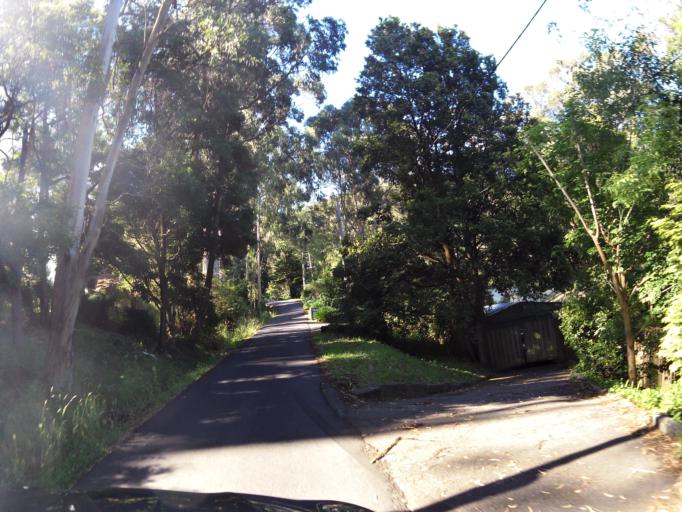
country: AU
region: Victoria
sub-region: Yarra Ranges
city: Tremont
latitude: -37.8967
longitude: 145.3396
